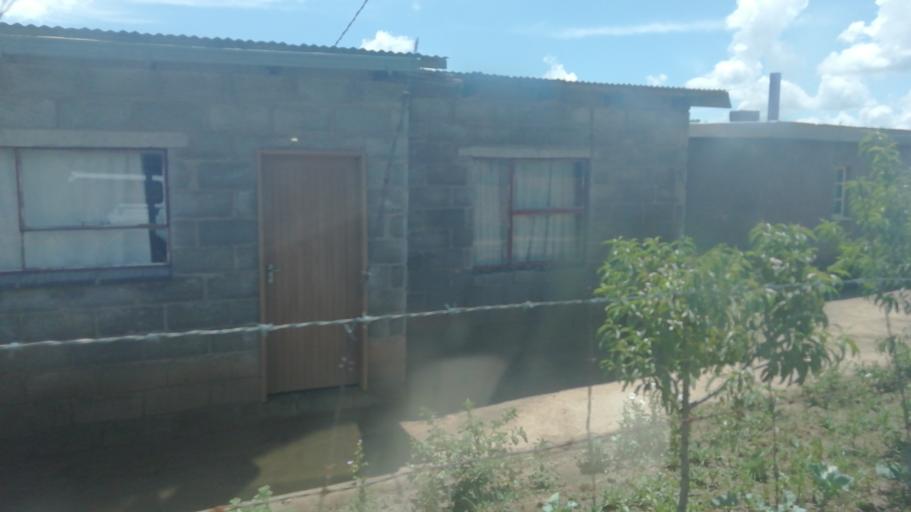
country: LS
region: Maseru
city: Nako
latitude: -29.6207
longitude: 27.5190
